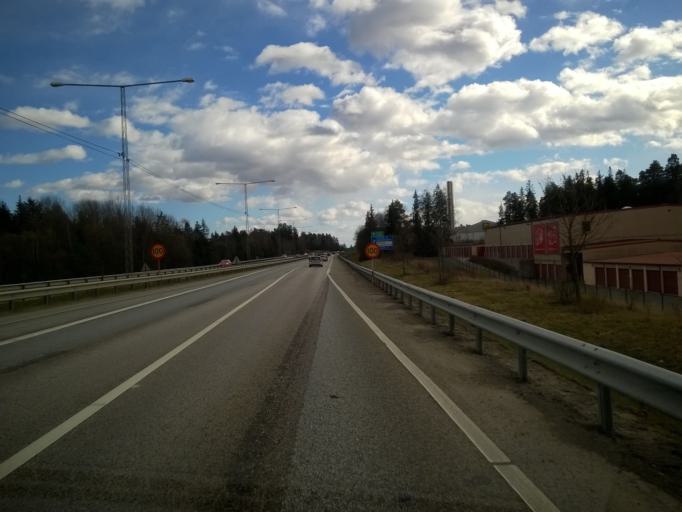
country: SE
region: Stockholm
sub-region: Jarfalla Kommun
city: Jakobsberg
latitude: 59.4314
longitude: 17.8472
